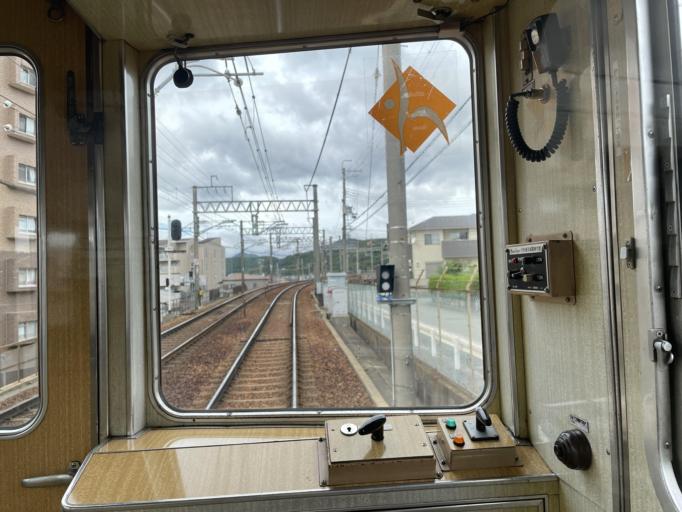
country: JP
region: Osaka
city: Ikeda
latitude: 34.8902
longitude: 135.4114
